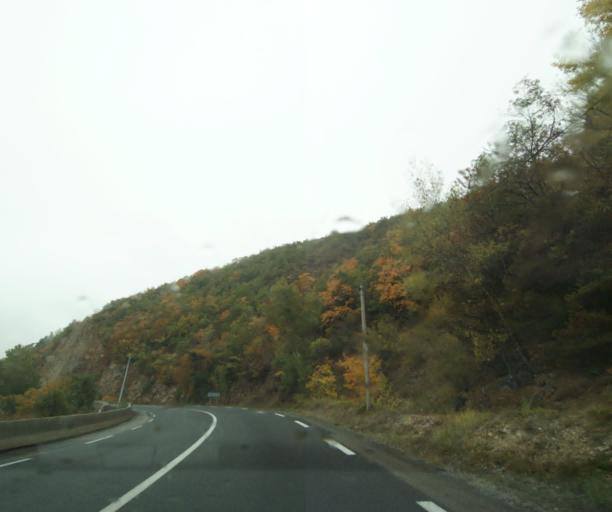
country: FR
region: Midi-Pyrenees
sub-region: Departement de l'Aveyron
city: Millau
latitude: 44.0903
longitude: 3.1247
